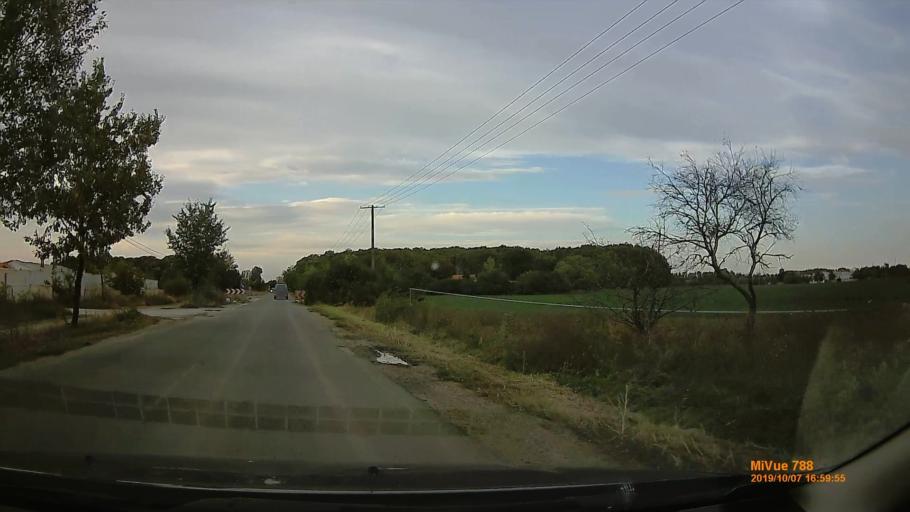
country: HU
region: Bekes
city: Szarvas
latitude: 46.8433
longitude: 20.5732
